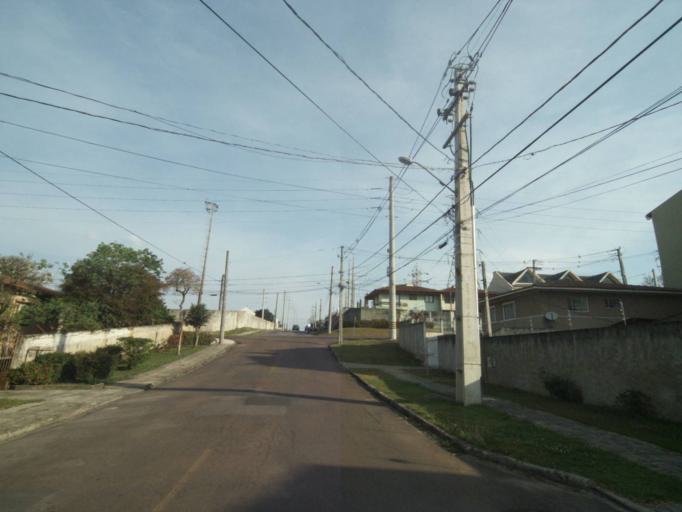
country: BR
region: Parana
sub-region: Curitiba
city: Curitiba
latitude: -25.4604
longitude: -49.3127
